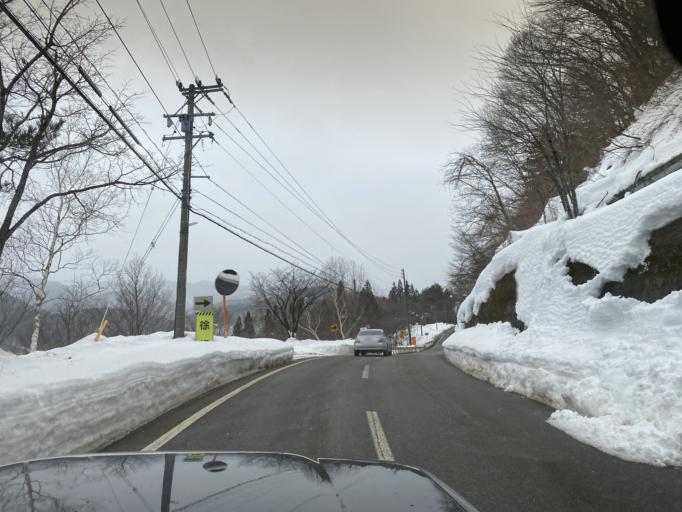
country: JP
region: Gifu
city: Takayama
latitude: 36.0879
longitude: 136.9426
